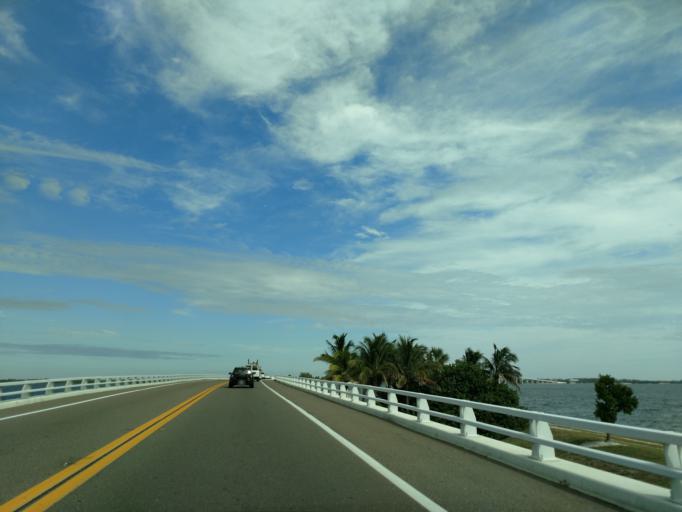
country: US
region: Florida
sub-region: Lee County
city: Sanibel
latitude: 26.4705
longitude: -82.0284
